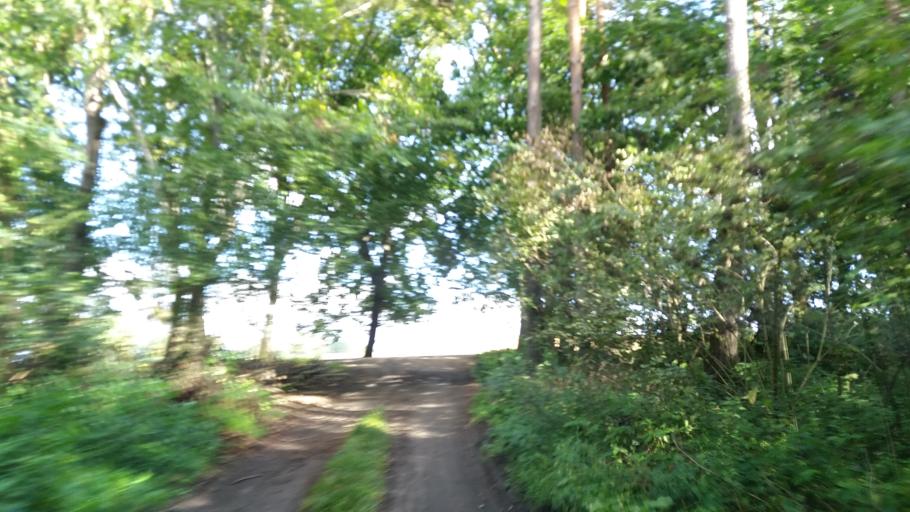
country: PL
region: West Pomeranian Voivodeship
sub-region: Powiat choszczenski
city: Krzecin
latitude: 53.1440
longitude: 15.4825
